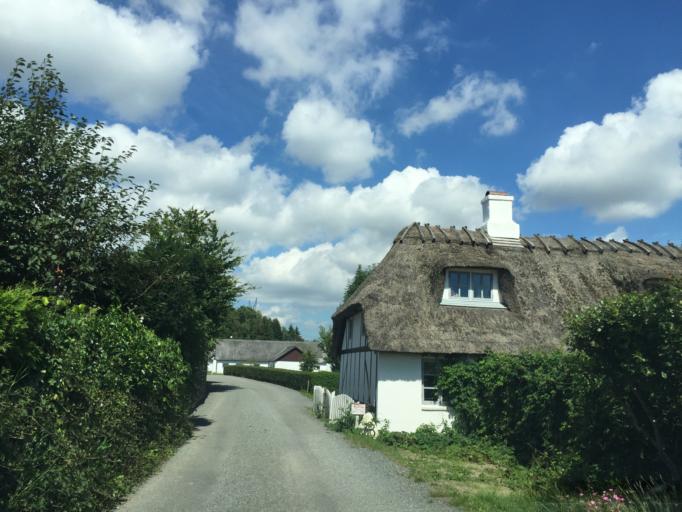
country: DK
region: South Denmark
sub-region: Odense Kommune
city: Hojby
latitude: 55.3448
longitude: 10.4268
